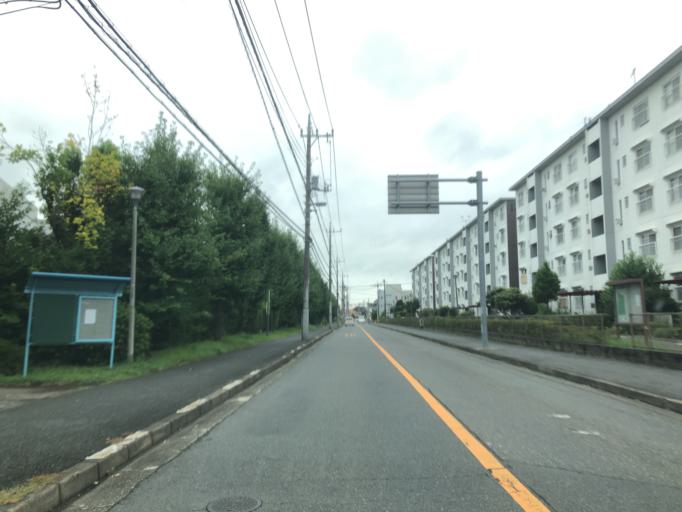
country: JP
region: Saitama
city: Sakado
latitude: 35.9766
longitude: 139.3945
